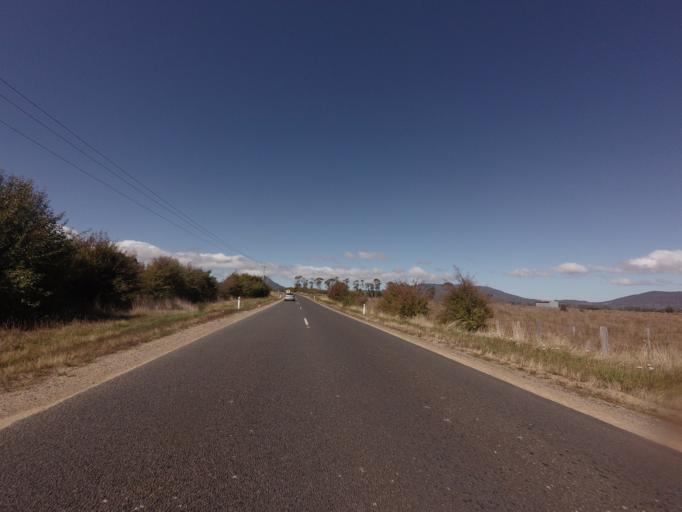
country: AU
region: Tasmania
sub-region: Break O'Day
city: St Helens
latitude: -41.5792
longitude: 148.1570
